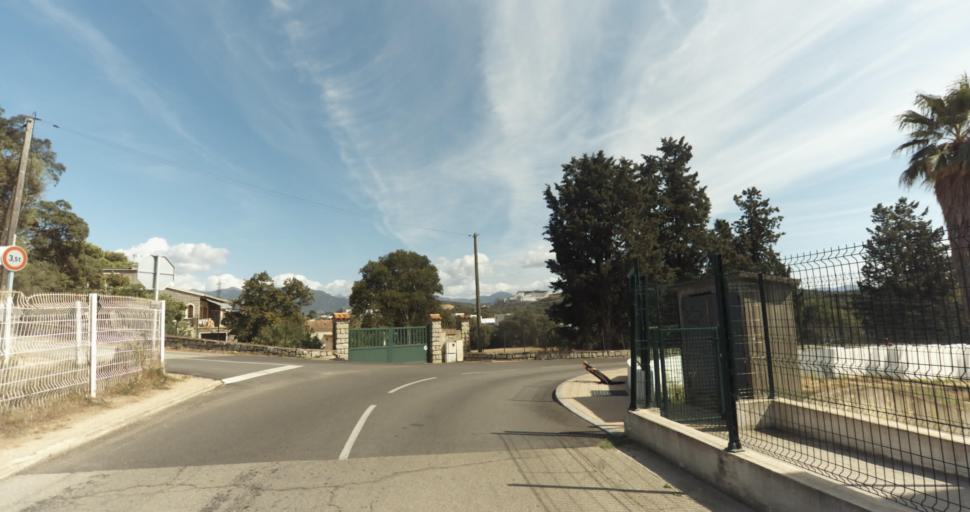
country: FR
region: Corsica
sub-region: Departement de la Corse-du-Sud
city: Ajaccio
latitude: 41.9487
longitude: 8.7572
